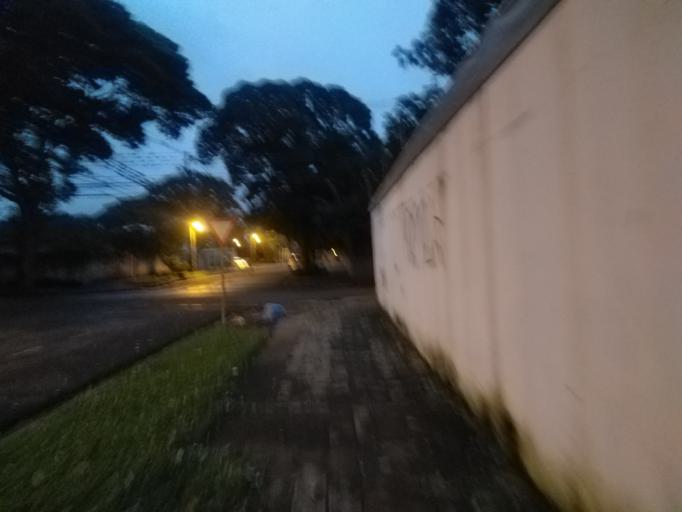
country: BR
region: Parana
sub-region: Maringa
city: Maringa
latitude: -23.4124
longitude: -51.9306
